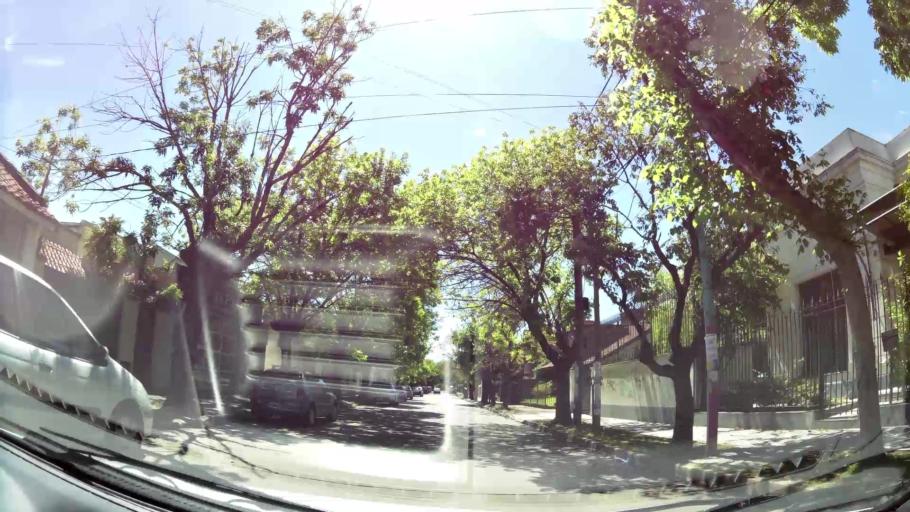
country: AR
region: Buenos Aires
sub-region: Partido de Quilmes
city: Quilmes
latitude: -34.7218
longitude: -58.2483
